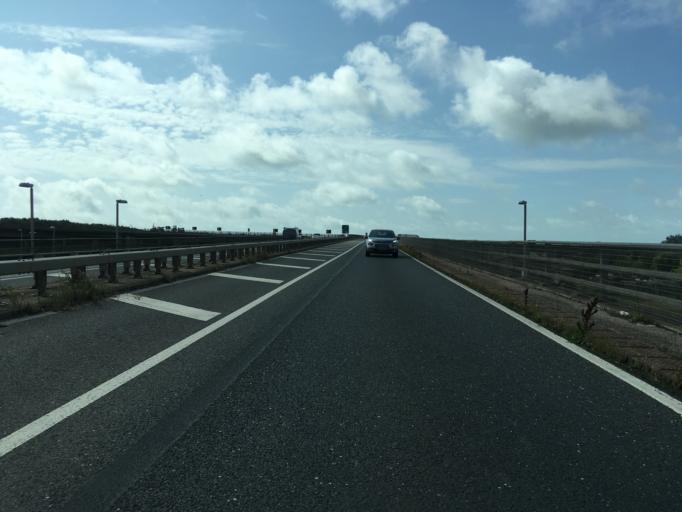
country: GB
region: England
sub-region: West Sussex
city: Shoreham-by-Sea
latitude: 50.8469
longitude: -0.2855
